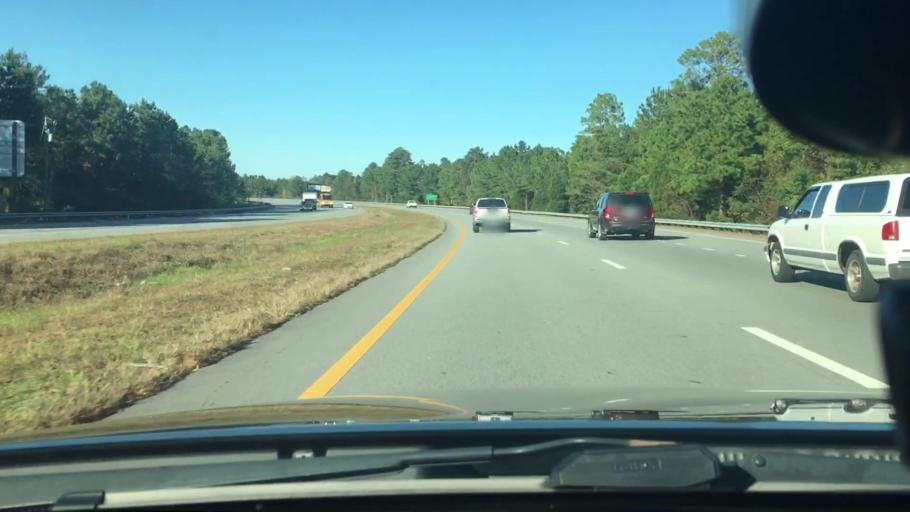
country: US
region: North Carolina
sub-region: Craven County
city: James City
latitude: 35.1048
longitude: -77.0089
